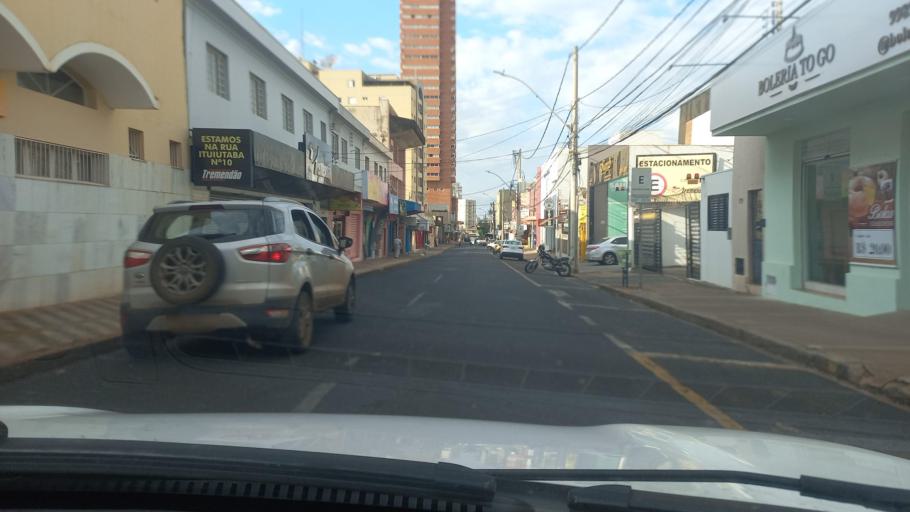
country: BR
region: Minas Gerais
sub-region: Uberaba
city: Uberaba
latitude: -19.7558
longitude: -47.9395
